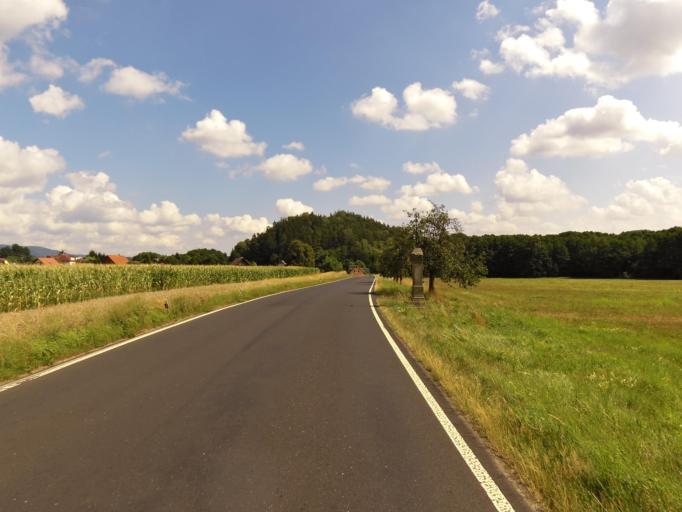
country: CZ
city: Osecna
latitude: 50.6991
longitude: 14.8992
